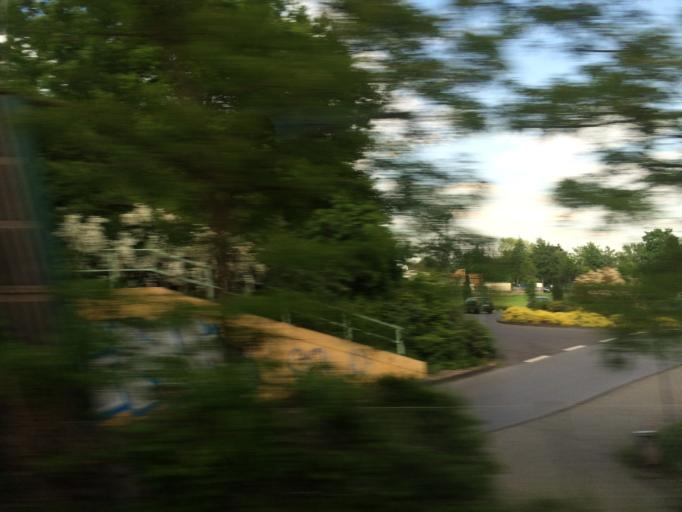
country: DE
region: North Rhine-Westphalia
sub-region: Regierungsbezirk Dusseldorf
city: Langenfeld
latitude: 51.1025
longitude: 6.9383
